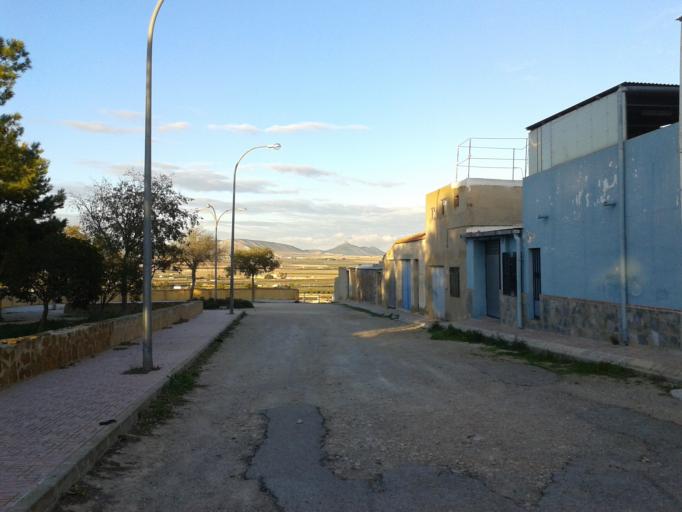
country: ES
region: Castille-La Mancha
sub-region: Provincia de Albacete
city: Caudete
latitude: 38.7053
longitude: -0.9915
